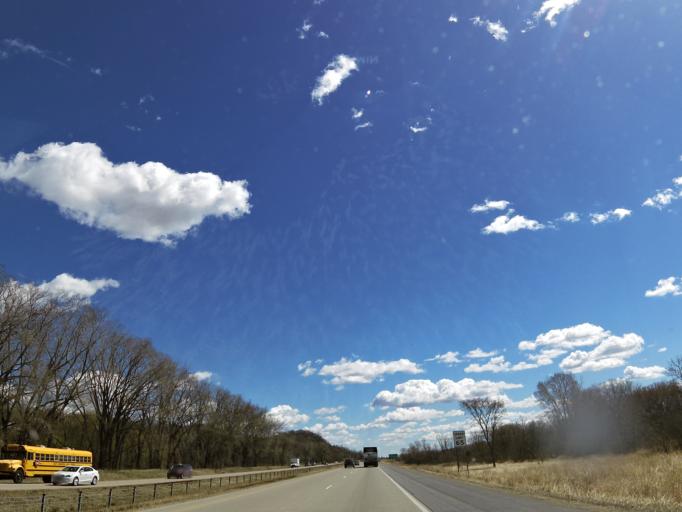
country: US
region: Minnesota
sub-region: Washington County
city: Saint Paul Park
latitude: 44.8447
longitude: -92.9803
